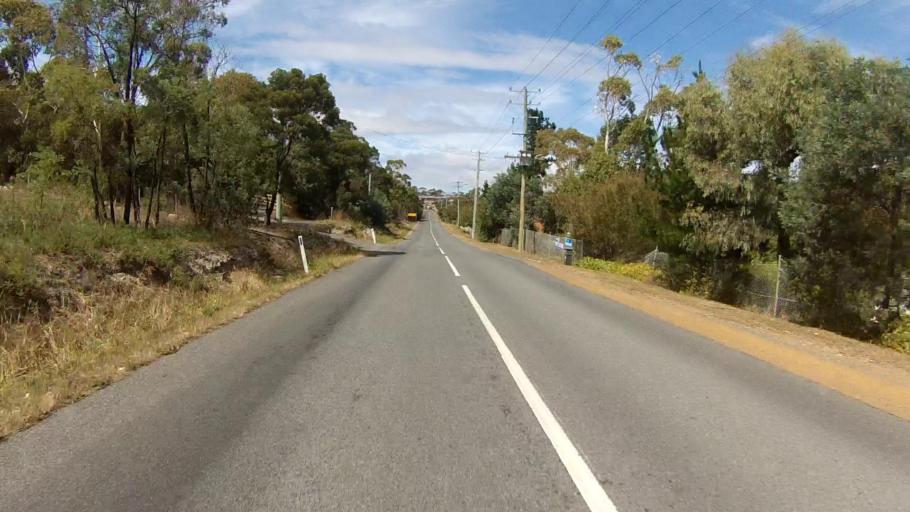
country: AU
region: Tasmania
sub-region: Clarence
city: Lindisfarne
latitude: -42.8170
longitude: 147.3513
